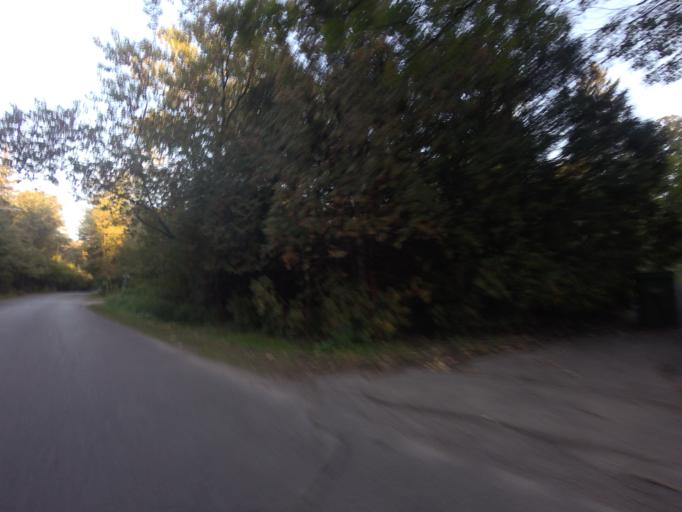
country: CA
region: Quebec
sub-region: Monteregie
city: Hudson
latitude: 45.4540
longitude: -74.1247
